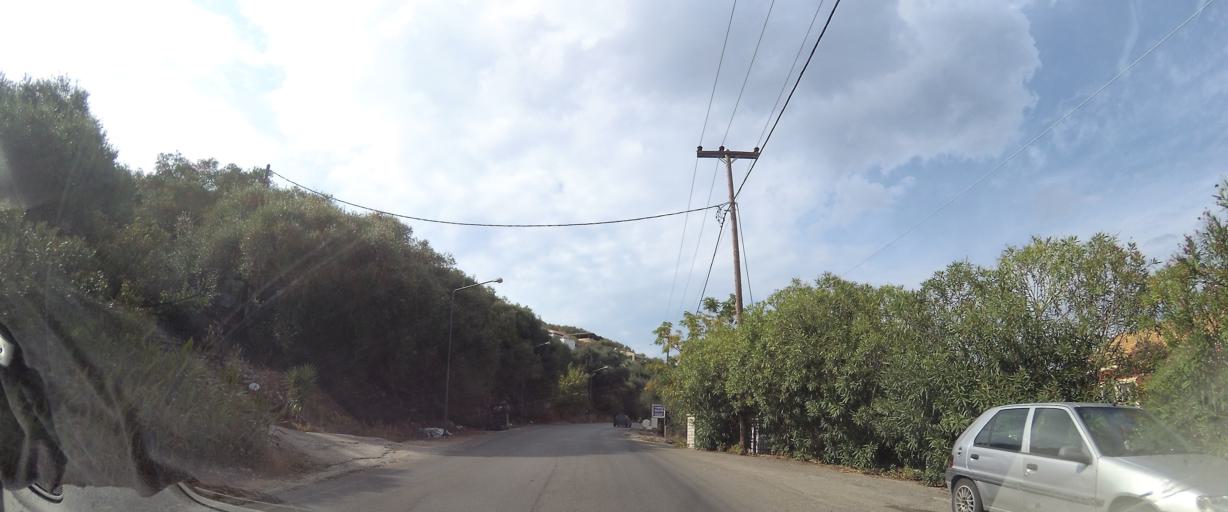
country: GR
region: Ionian Islands
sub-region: Nomos Kerkyras
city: Acharavi
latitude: 39.7971
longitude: 19.8847
